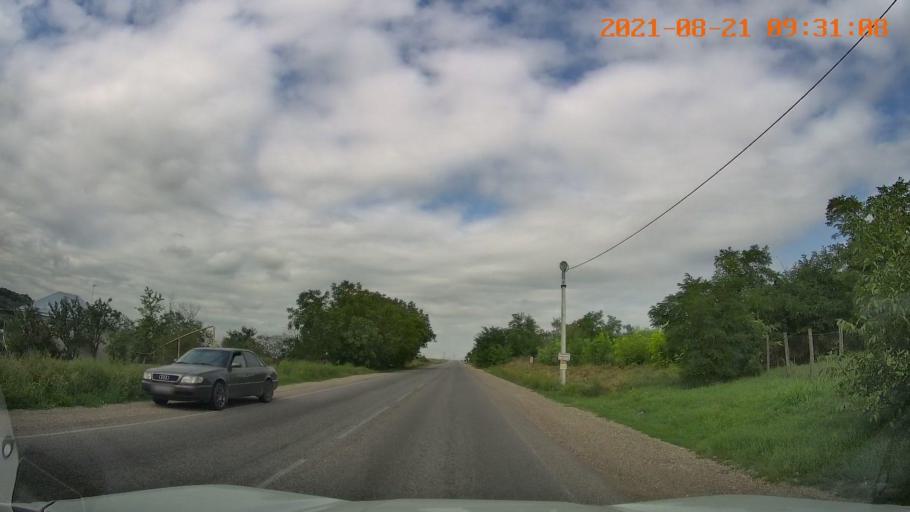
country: RU
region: Stavropol'skiy
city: Yutsa
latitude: 43.9901
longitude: 43.0300
